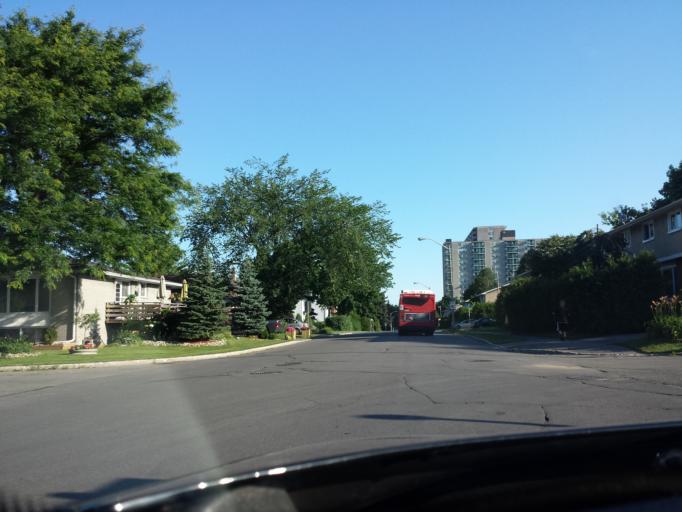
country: CA
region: Ontario
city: Bells Corners
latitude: 45.3631
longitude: -75.7919
